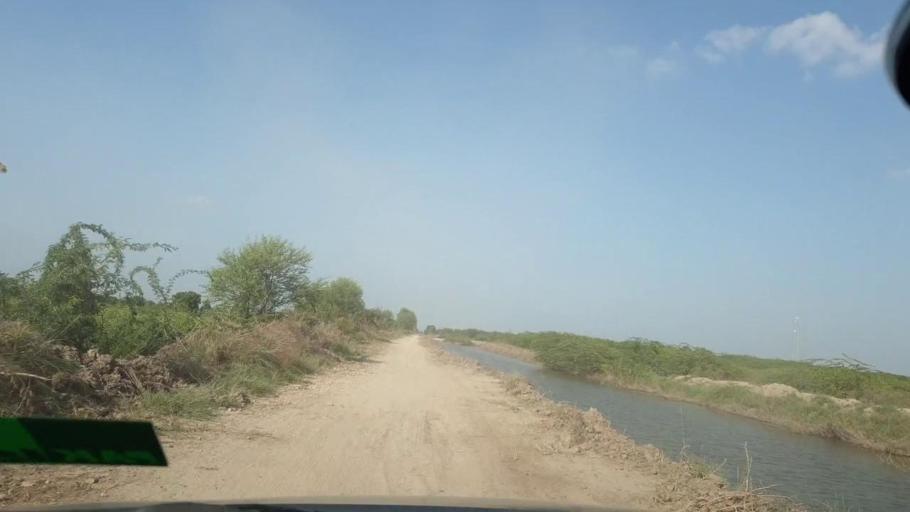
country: PK
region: Sindh
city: Naukot
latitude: 24.7078
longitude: 69.2041
